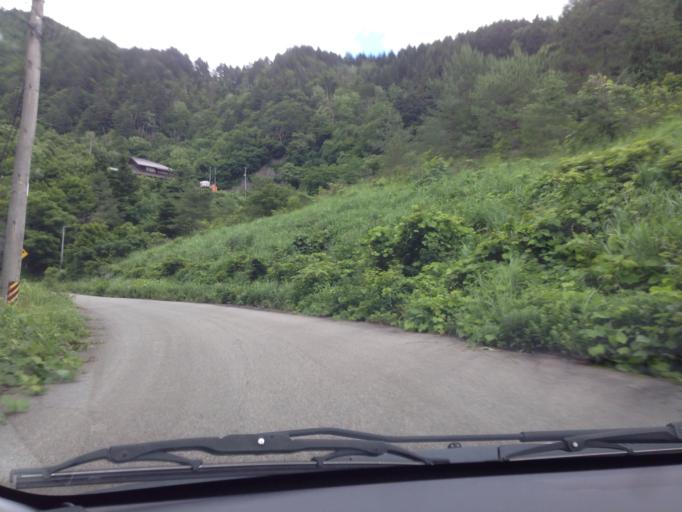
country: JP
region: Fukushima
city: Kitakata
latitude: 37.7540
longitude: 139.9020
